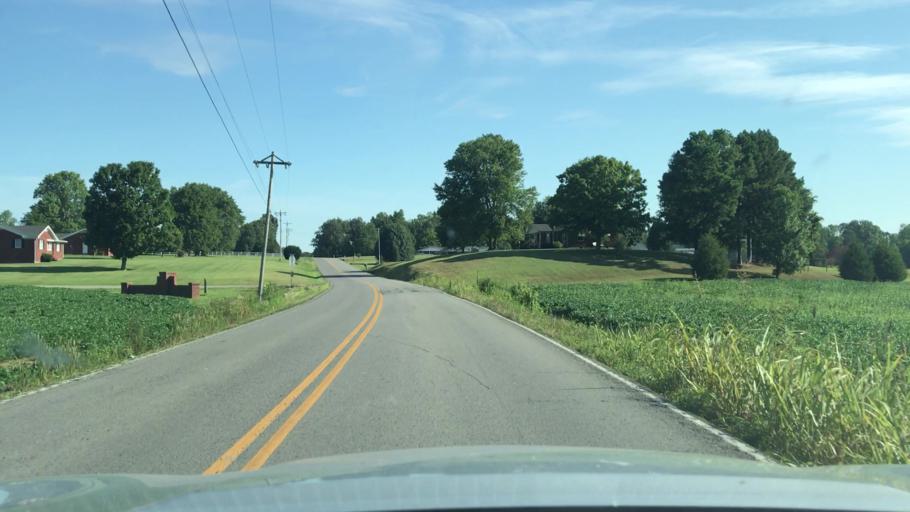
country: US
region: Kentucky
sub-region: Muhlenberg County
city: Greenville
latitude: 37.1453
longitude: -87.1411
